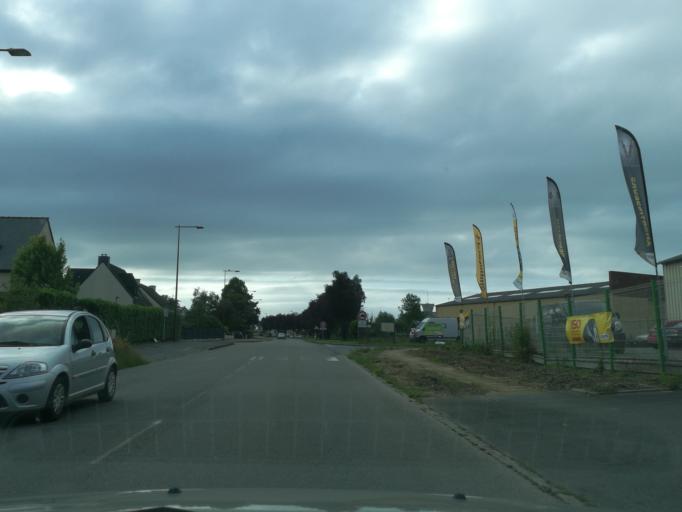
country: FR
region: Brittany
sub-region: Departement d'Ille-et-Vilaine
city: Bedee
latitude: 48.1788
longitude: -1.9333
